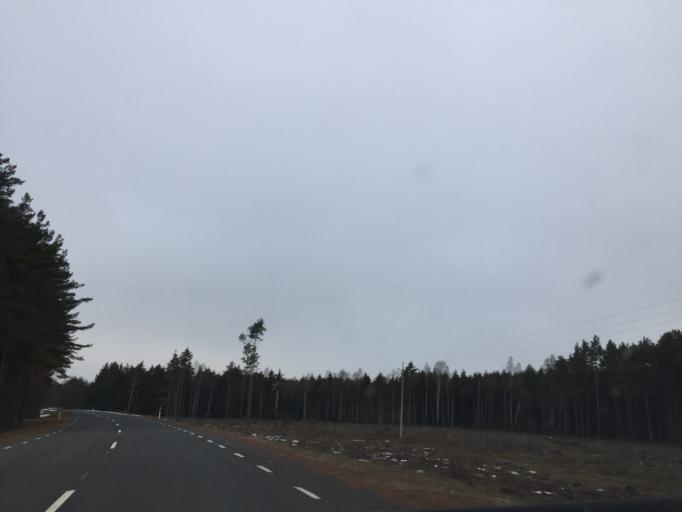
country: EE
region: Saare
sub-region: Kuressaare linn
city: Kuressaare
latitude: 58.5520
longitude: 22.3262
